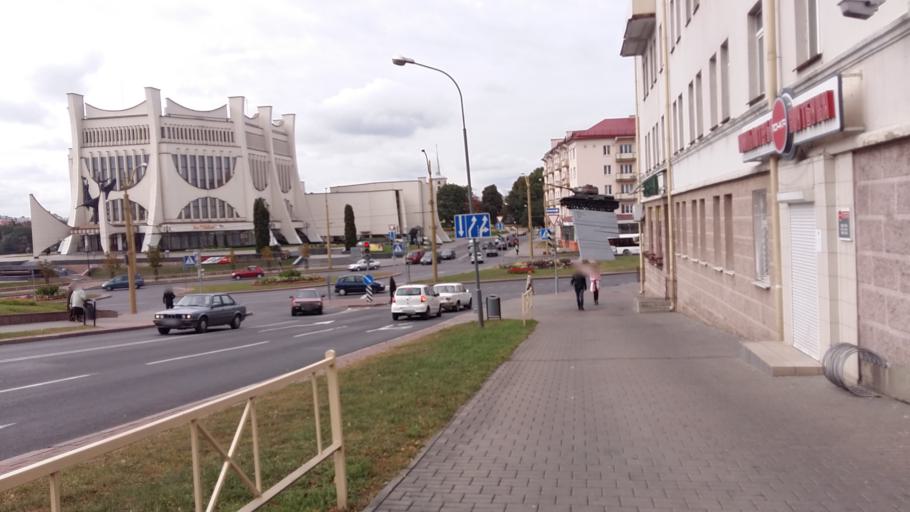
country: BY
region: Grodnenskaya
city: Hrodna
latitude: 53.6756
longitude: 23.8300
